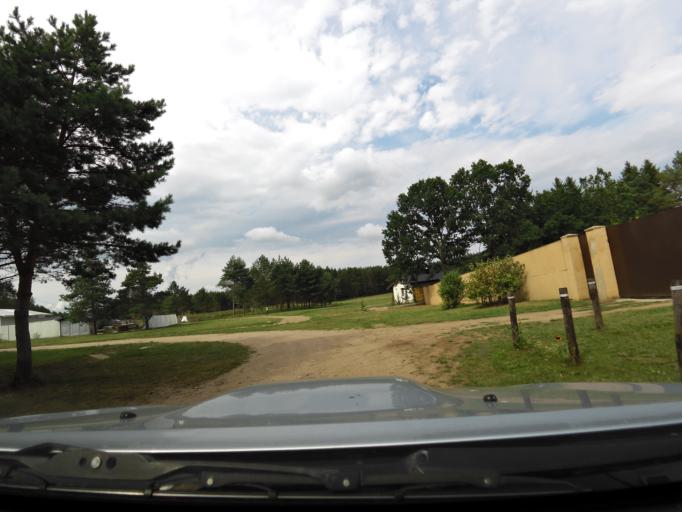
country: LT
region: Vilnius County
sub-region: Vilniaus Rajonas
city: Vievis
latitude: 54.9232
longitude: 24.7566
